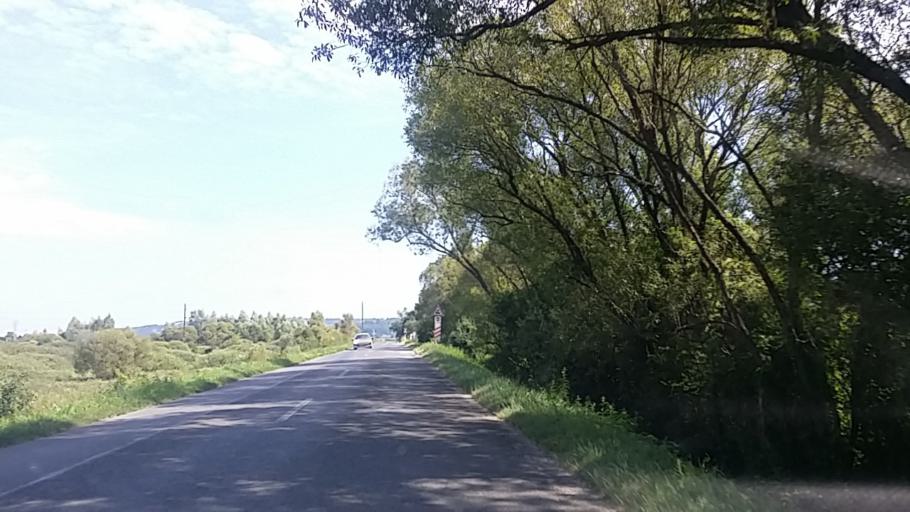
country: HU
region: Baranya
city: Sasd
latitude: 46.2151
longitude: 18.1052
